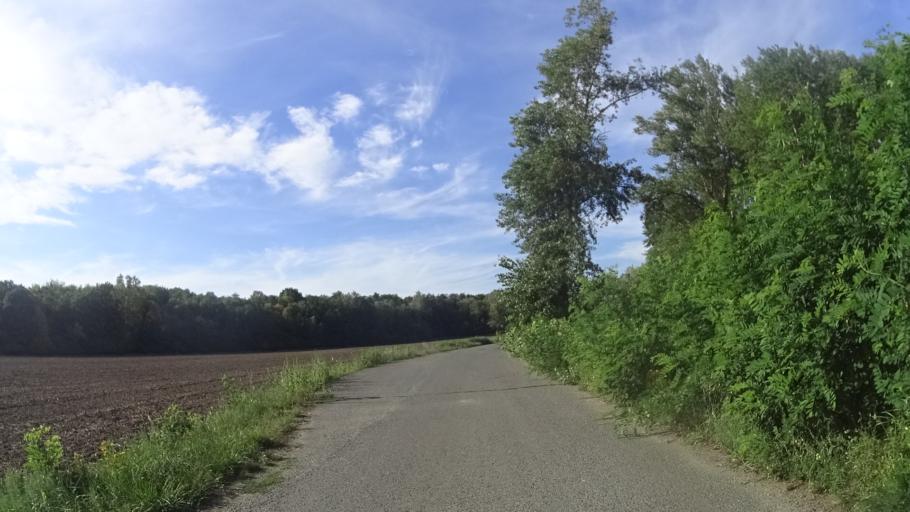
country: AT
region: Lower Austria
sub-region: Politischer Bezirk Ganserndorf
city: Drosing
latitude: 48.5950
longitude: 16.9499
